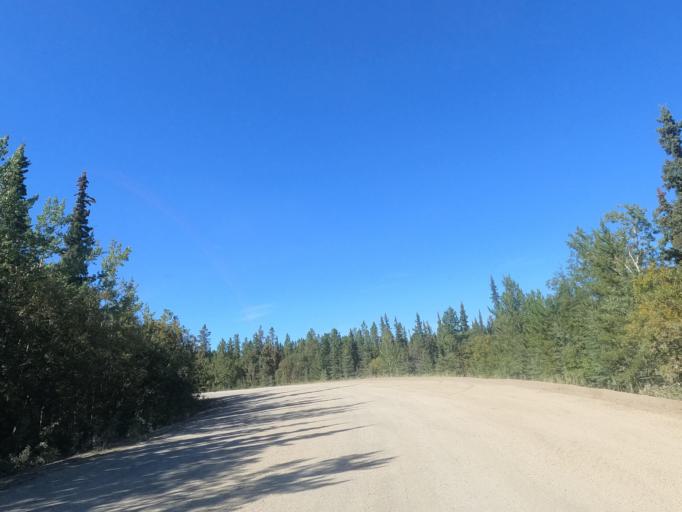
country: CA
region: Yukon
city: Whitehorse
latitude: 60.6634
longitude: -135.0323
